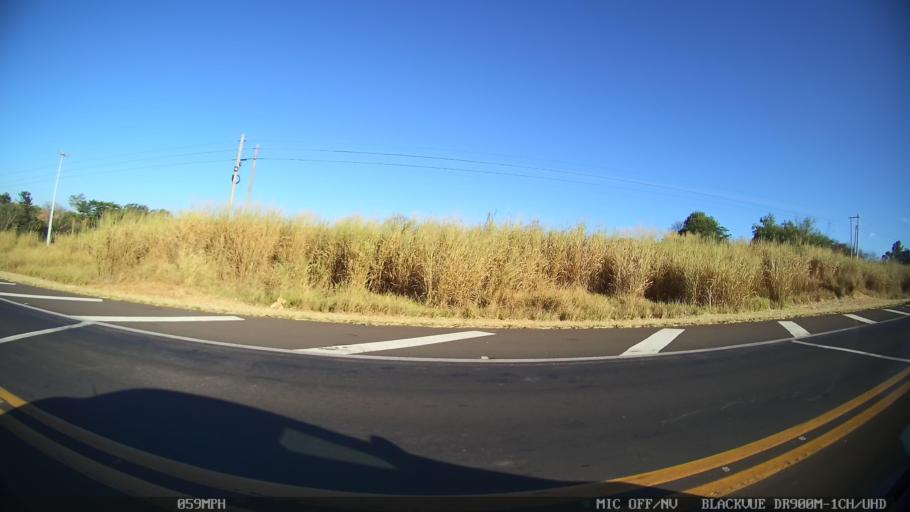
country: BR
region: Sao Paulo
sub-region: Olimpia
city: Olimpia
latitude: -20.7029
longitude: -48.9453
